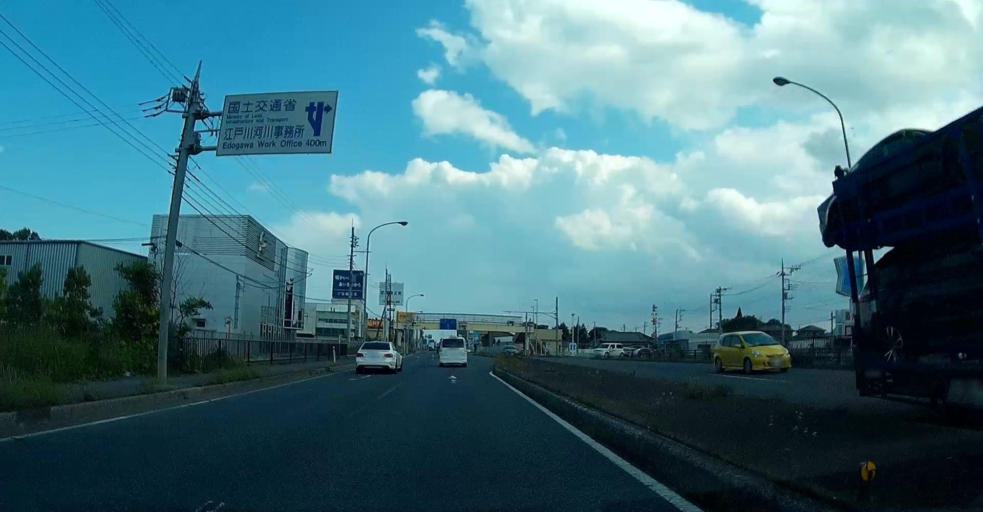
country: JP
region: Chiba
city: Noda
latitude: 35.9631
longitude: 139.8698
